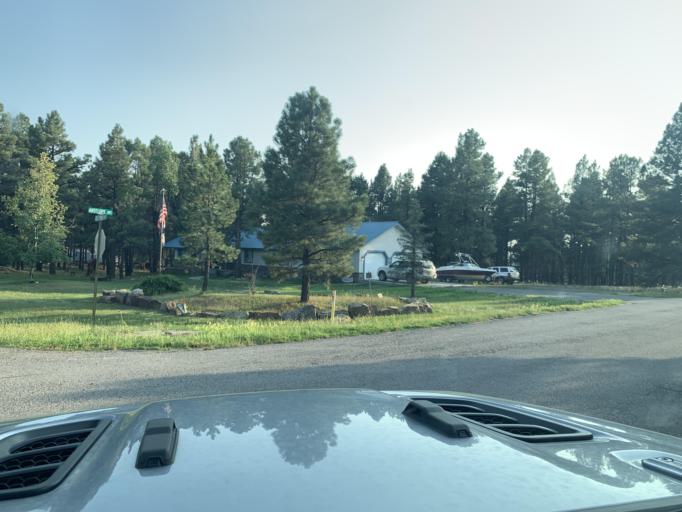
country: US
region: Colorado
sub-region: Archuleta County
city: Pagosa Springs
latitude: 37.2641
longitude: -107.0946
